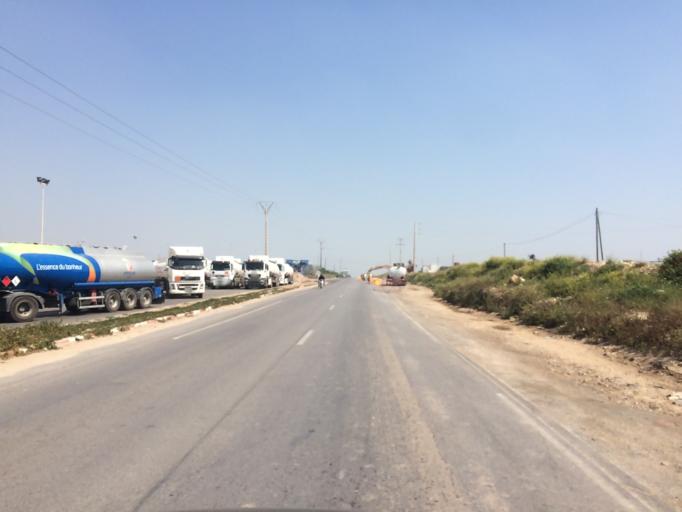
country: MA
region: Doukkala-Abda
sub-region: El-Jadida
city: Moulay Abdallah
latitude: 33.1459
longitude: -8.6071
